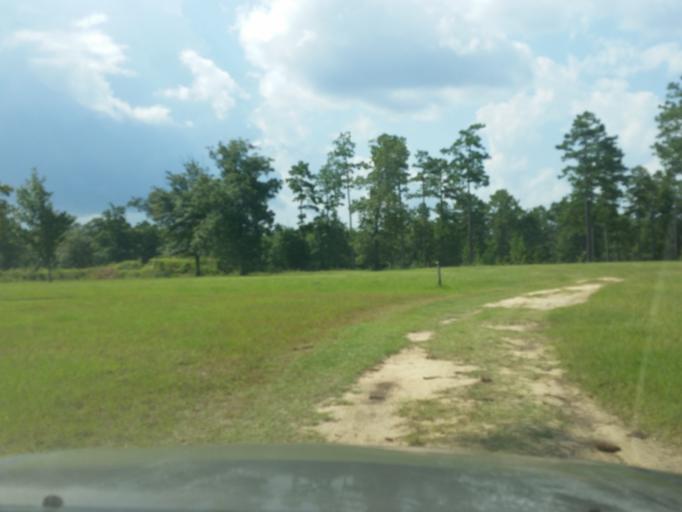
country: US
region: Alabama
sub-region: Baldwin County
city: Spanish Fort
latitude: 30.7484
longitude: -87.9109
